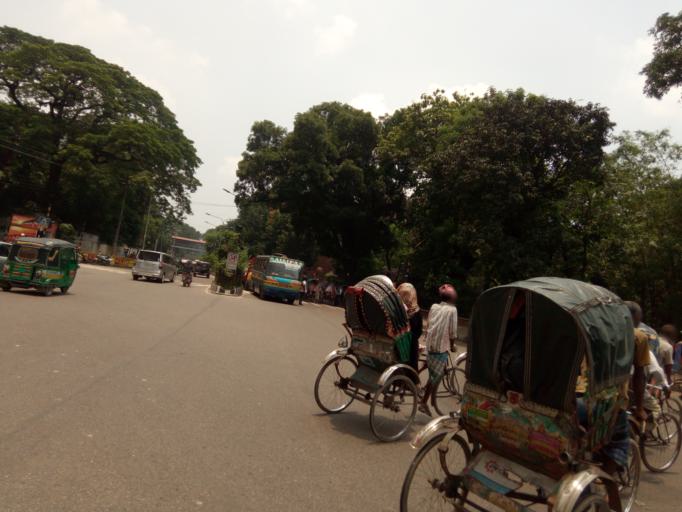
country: BD
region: Dhaka
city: Paltan
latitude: 23.7283
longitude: 90.4040
